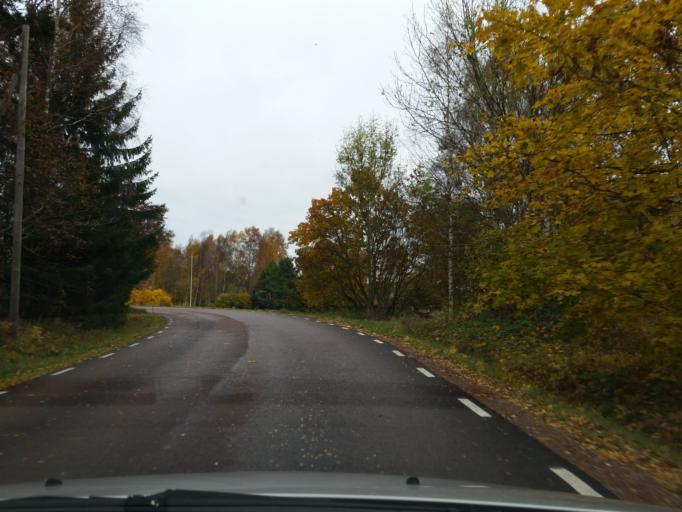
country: AX
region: Alands landsbygd
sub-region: Lemland
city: Lemland
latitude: 60.0754
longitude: 20.0834
